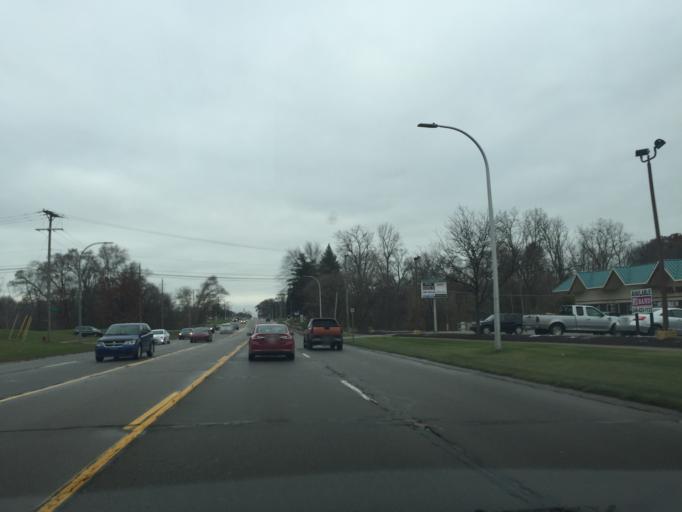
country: US
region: Michigan
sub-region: Wayne County
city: Livonia
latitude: 42.4102
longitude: -83.3352
